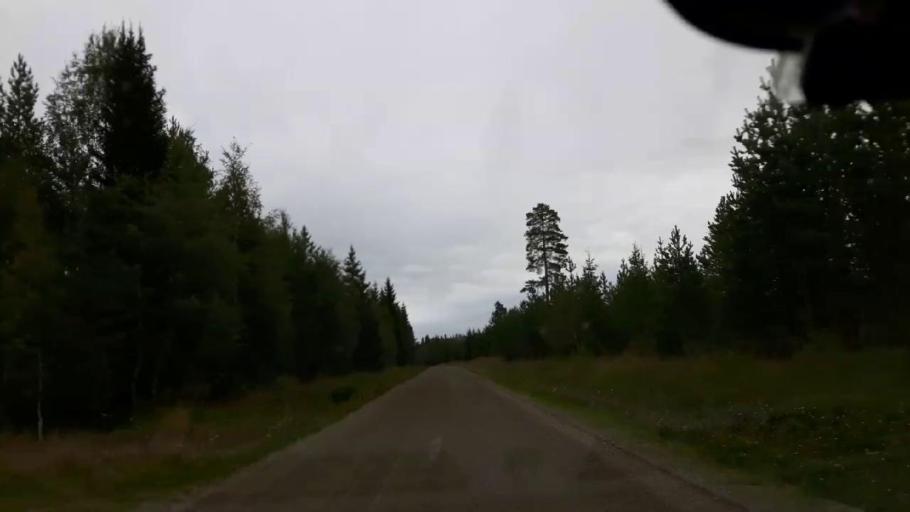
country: SE
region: Jaemtland
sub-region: Braecke Kommun
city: Braecke
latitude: 62.9397
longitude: 15.4551
